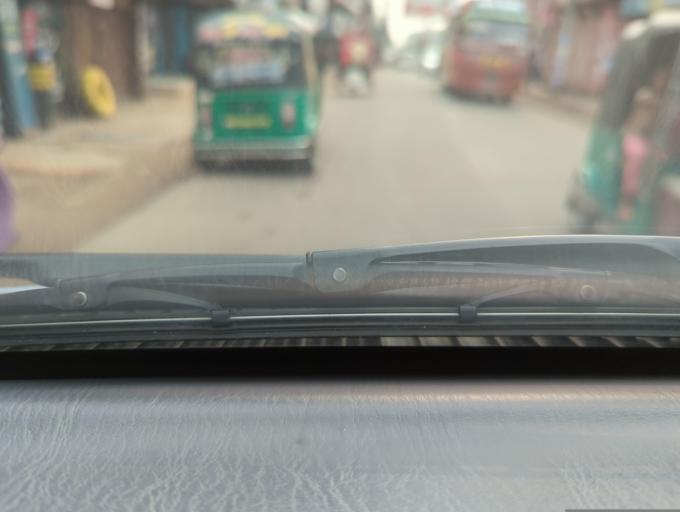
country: BD
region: Sylhet
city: Maulavi Bazar
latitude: 24.4846
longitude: 91.7656
